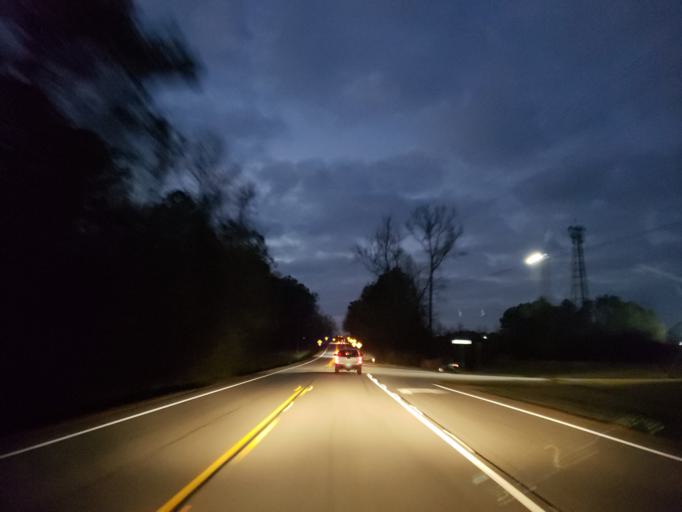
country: US
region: Georgia
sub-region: Polk County
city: Rockmart
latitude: 33.9210
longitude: -84.9925
